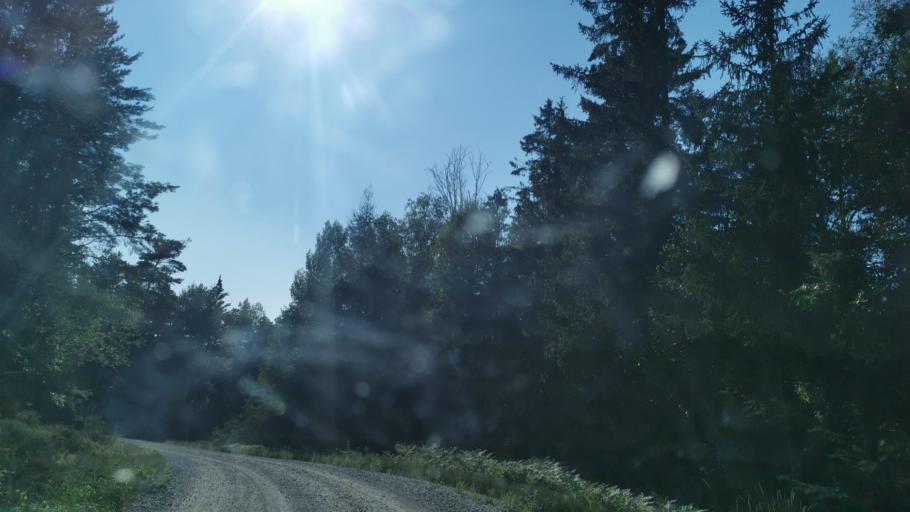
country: SE
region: OEstergoetland
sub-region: Norrkopings Kommun
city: Jursla
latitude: 58.7109
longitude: 16.1722
